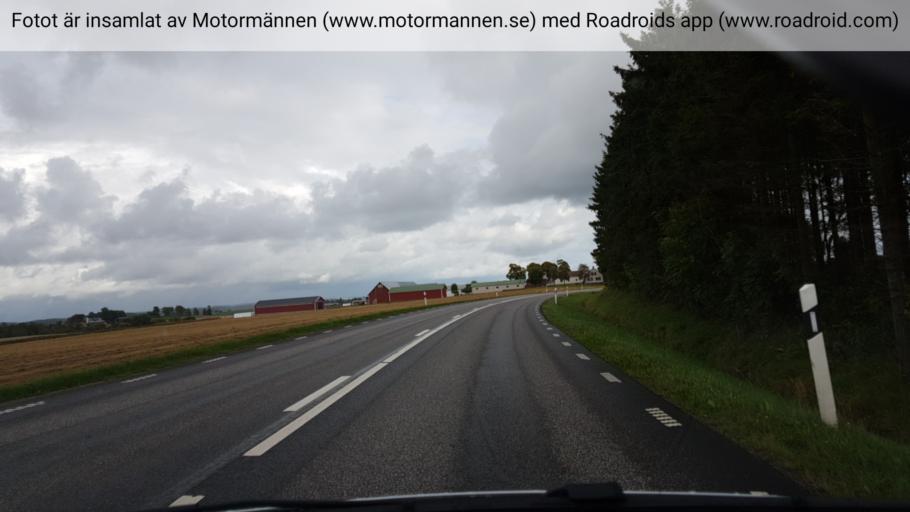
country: SE
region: Vaestra Goetaland
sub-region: Falkopings Kommun
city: Akarp
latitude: 58.0879
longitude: 13.7478
